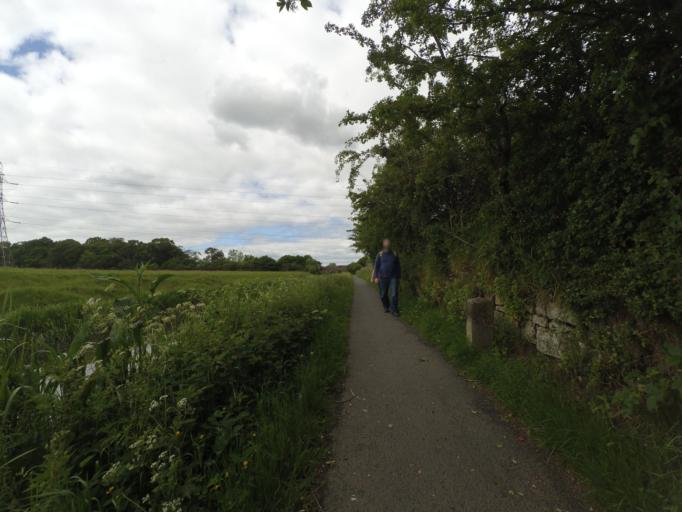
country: GB
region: Scotland
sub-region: Falkirk
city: Polmont
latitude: 55.9819
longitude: -3.6965
